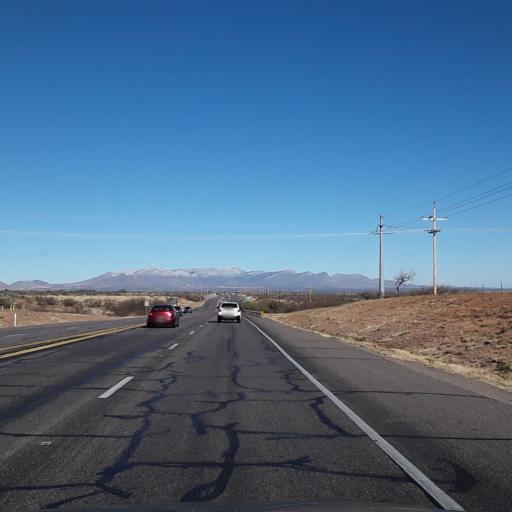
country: US
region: Arizona
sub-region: Cochise County
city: Sierra Vista
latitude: 31.5677
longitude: -110.3123
